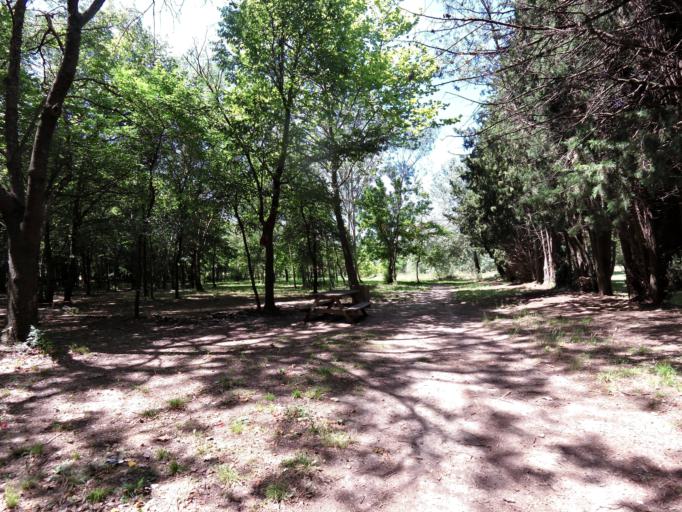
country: FR
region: Languedoc-Roussillon
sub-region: Departement du Gard
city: Caissargues
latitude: 43.7839
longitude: 4.3492
